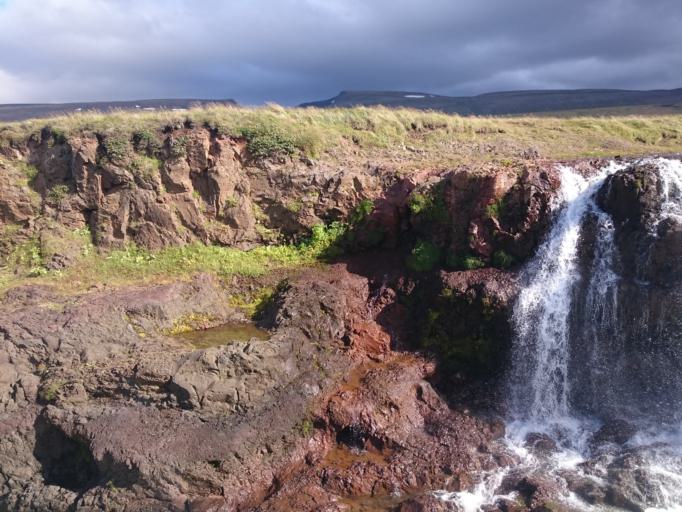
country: IS
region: Northwest
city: Saudarkrokur
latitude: 65.3320
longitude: -20.5701
